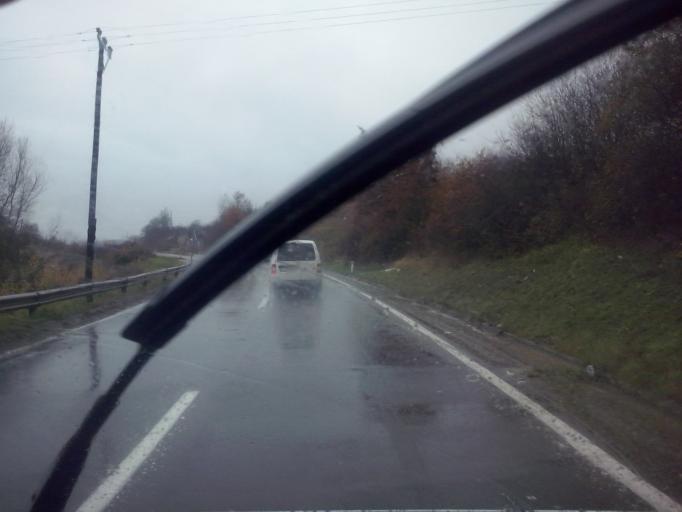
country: RS
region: Central Serbia
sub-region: Raski Okrug
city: Raska
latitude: 43.2365
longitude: 20.5841
